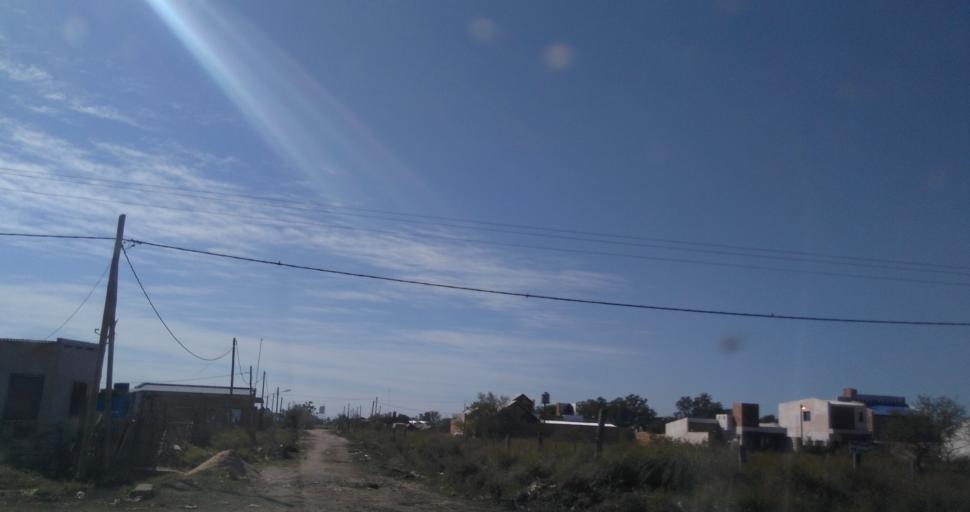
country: AR
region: Chaco
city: Fontana
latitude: -27.4594
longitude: -59.0456
